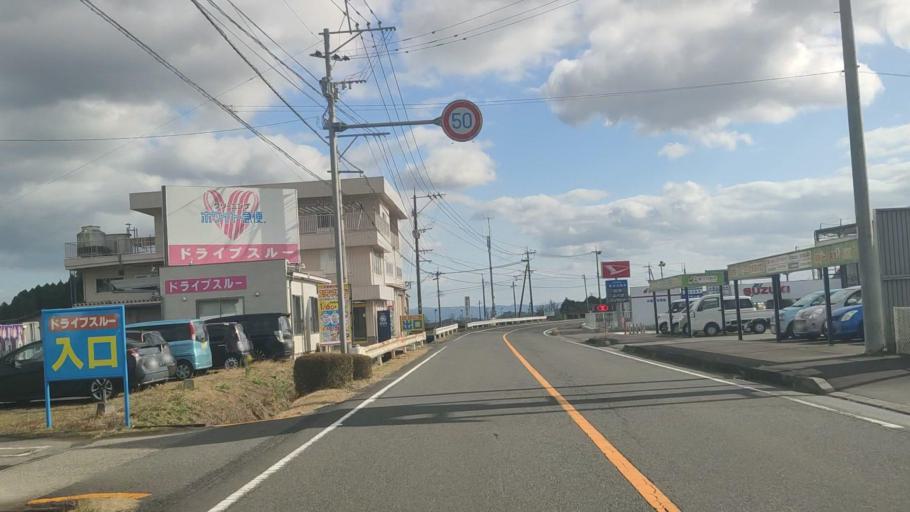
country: JP
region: Kagoshima
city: Kajiki
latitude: 31.8192
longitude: 130.7040
